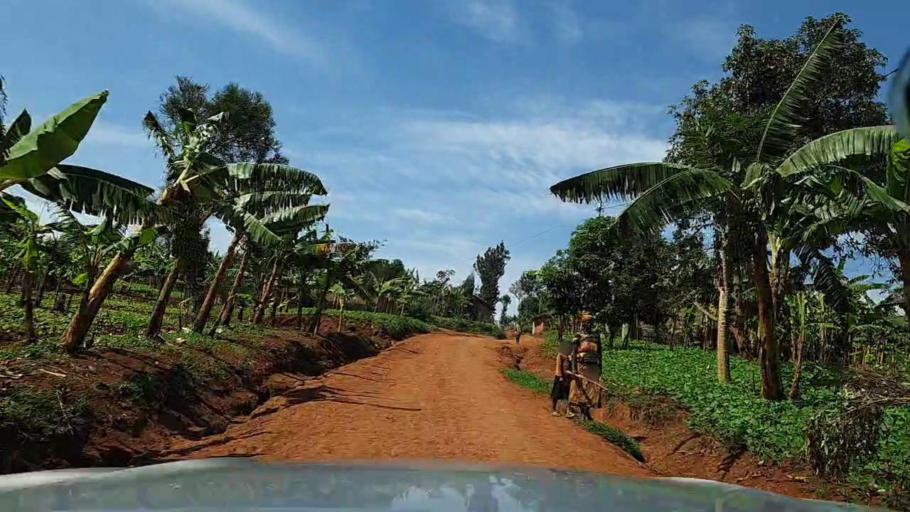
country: RW
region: Southern Province
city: Butare
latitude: -2.7005
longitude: 29.8506
